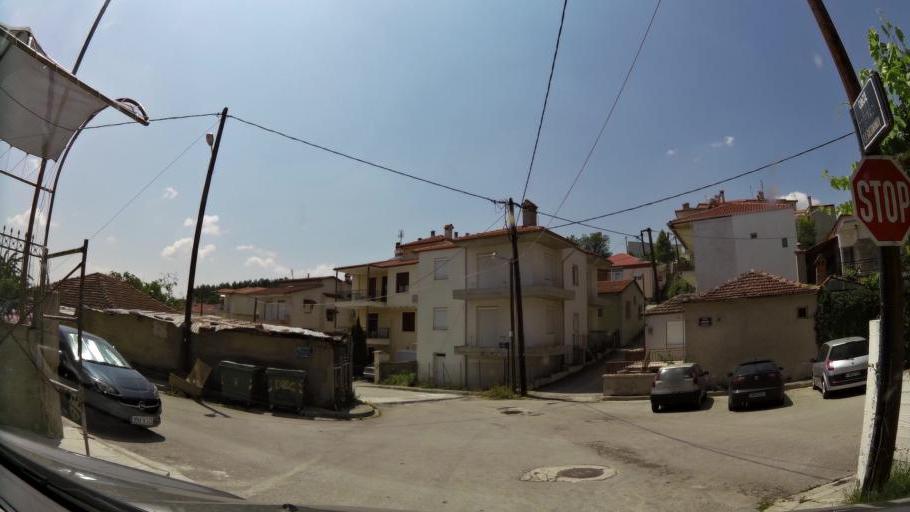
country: GR
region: West Macedonia
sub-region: Nomos Kozanis
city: Kozani
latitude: 40.3006
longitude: 21.7781
